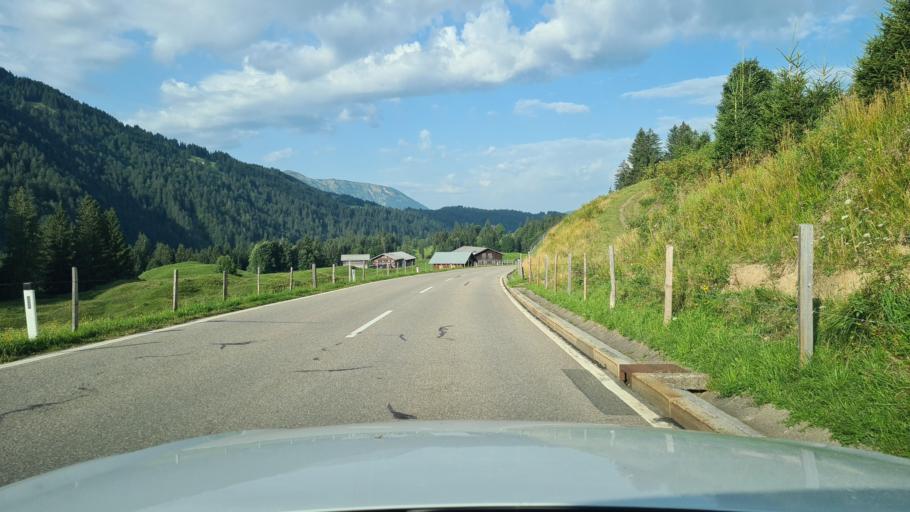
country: AT
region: Vorarlberg
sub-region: Politischer Bezirk Bregenz
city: Sibratsgfall
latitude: 47.4542
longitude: 10.0540
